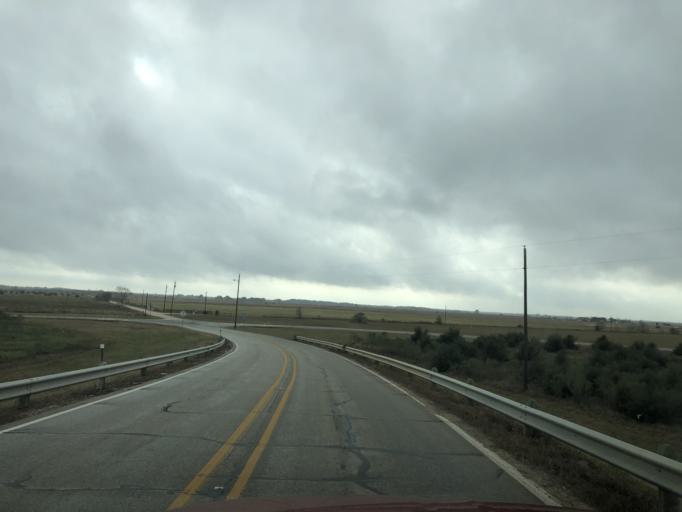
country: US
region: Texas
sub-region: Austin County
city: Sealy
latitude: 29.7582
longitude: -96.2203
